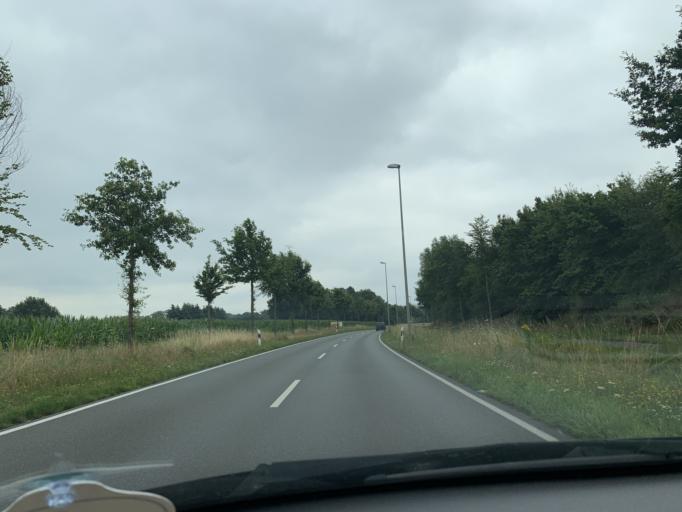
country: DE
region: North Rhine-Westphalia
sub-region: Regierungsbezirk Munster
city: Warendorf
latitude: 51.9612
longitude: 8.0070
